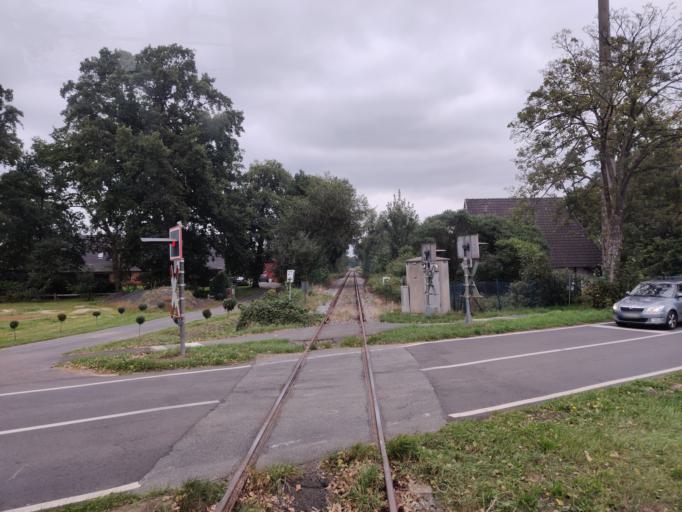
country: DE
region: Lower Saxony
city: Vollersode
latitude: 53.3132
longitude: 8.9749
